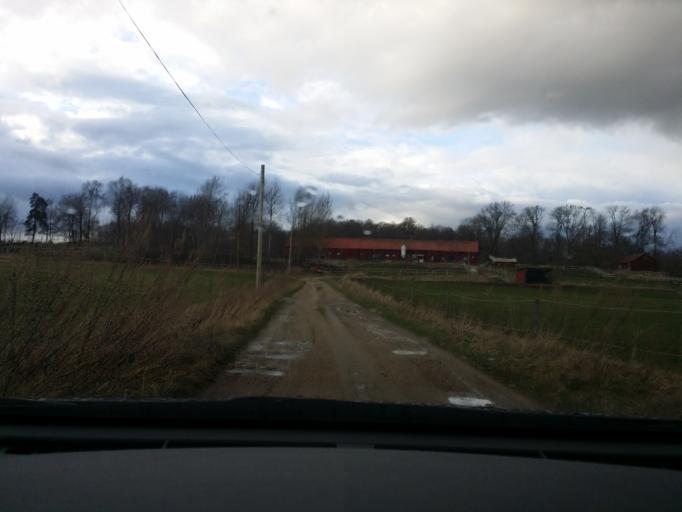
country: SE
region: Soedermanland
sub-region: Eskilstuna Kommun
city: Arla
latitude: 59.3773
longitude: 16.6511
